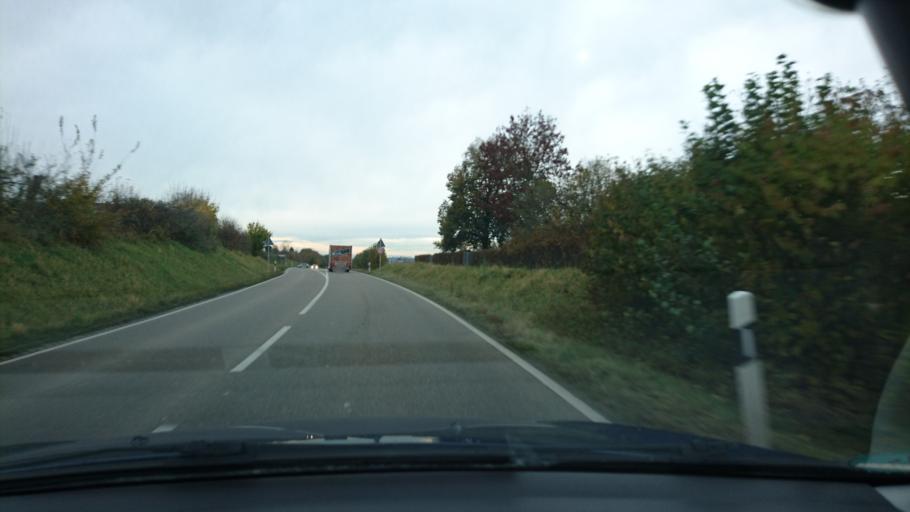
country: DE
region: Baden-Wuerttemberg
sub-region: Regierungsbezirk Stuttgart
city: Welzheim
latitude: 48.8821
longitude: 9.6220
